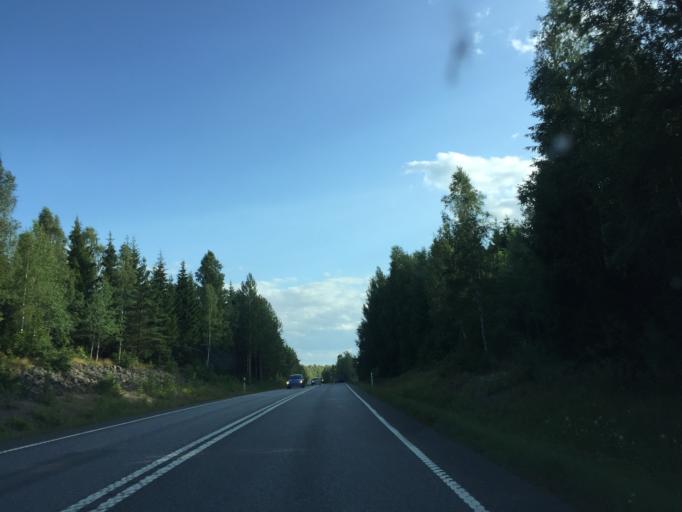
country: SE
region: OEstergoetland
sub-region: Motala Kommun
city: Ryd
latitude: 58.6604
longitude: 14.9645
